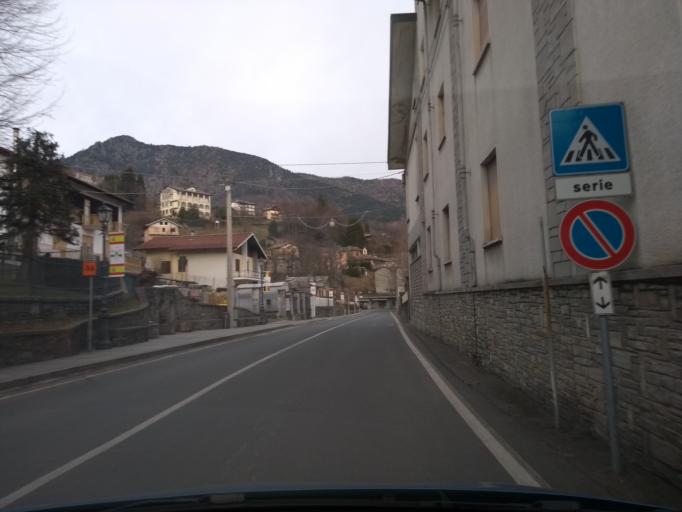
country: IT
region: Piedmont
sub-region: Provincia di Torino
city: Viu
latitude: 45.2378
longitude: 7.3714
